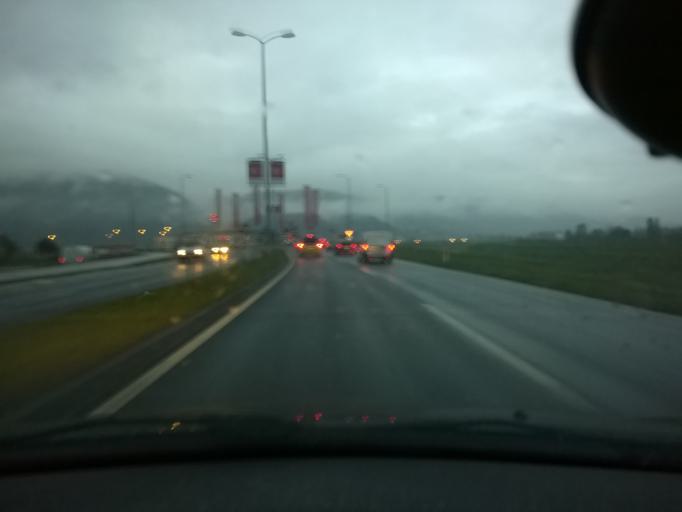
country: HR
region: Zagrebacka
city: Zapresic
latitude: 45.8692
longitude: 15.8241
